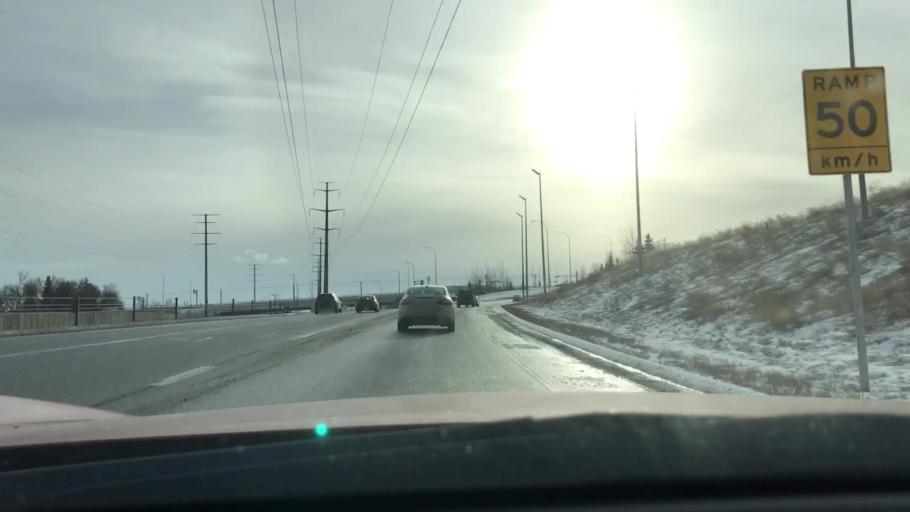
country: CA
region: Alberta
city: Calgary
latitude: 51.0435
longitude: -114.1645
